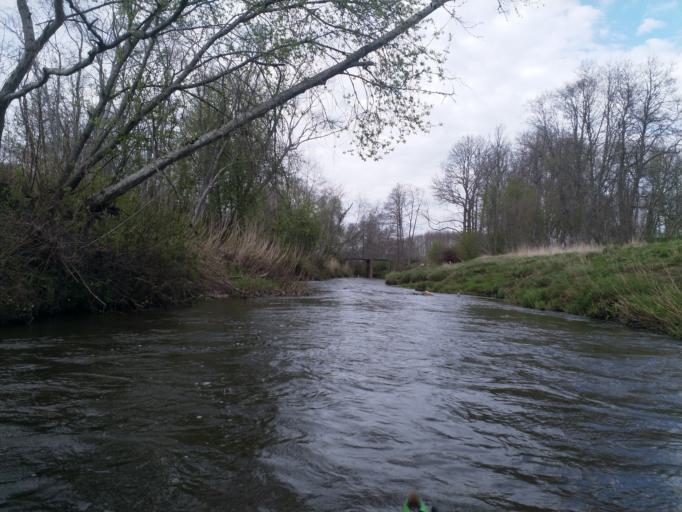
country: LV
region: Alsunga
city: Alsunga
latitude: 57.1247
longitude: 21.5495
